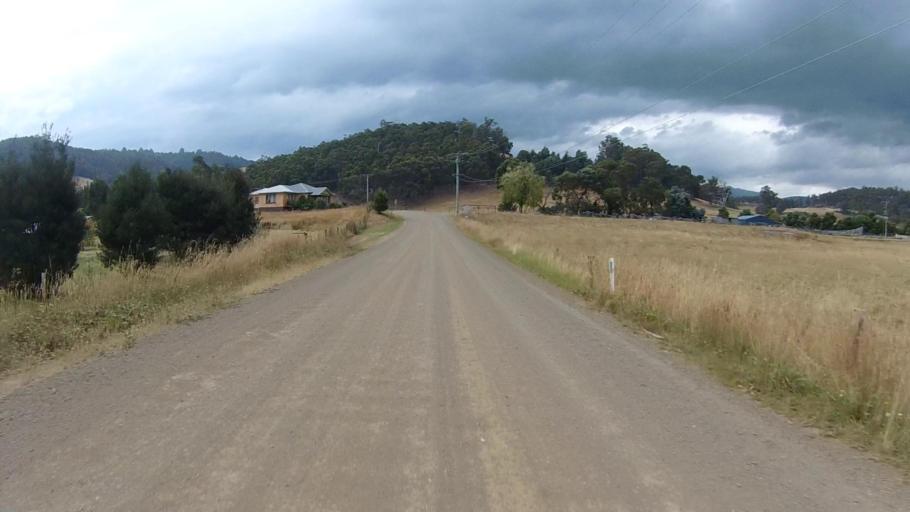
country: AU
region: Tasmania
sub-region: Huon Valley
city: Huonville
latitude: -42.9791
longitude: 147.0547
